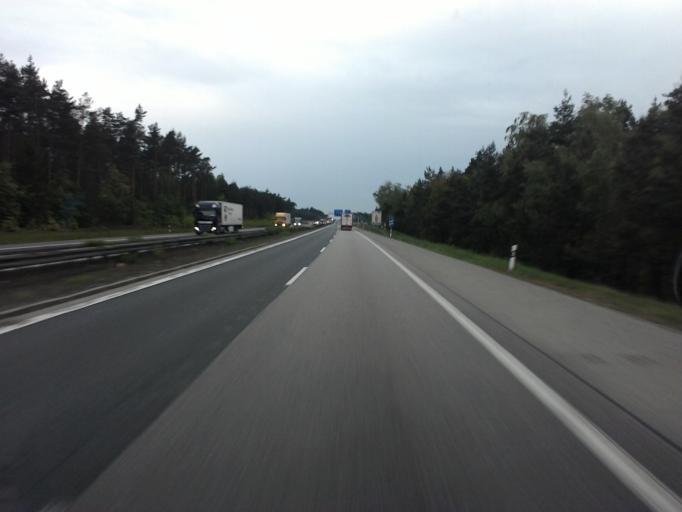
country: DE
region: Bavaria
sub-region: Regierungsbezirk Mittelfranken
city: Rothenbach an der Pegnitz
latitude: 49.4535
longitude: 11.2572
